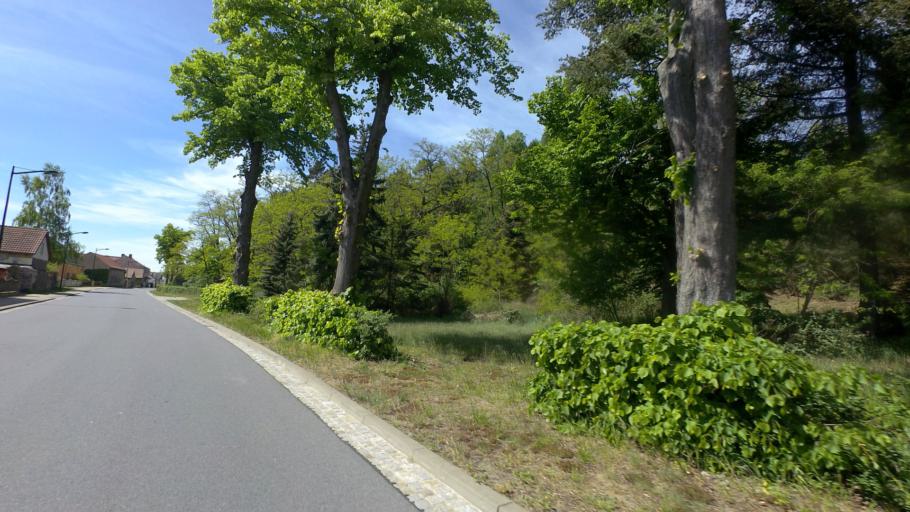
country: DE
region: Brandenburg
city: Sperenberg
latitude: 52.0836
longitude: 13.4049
